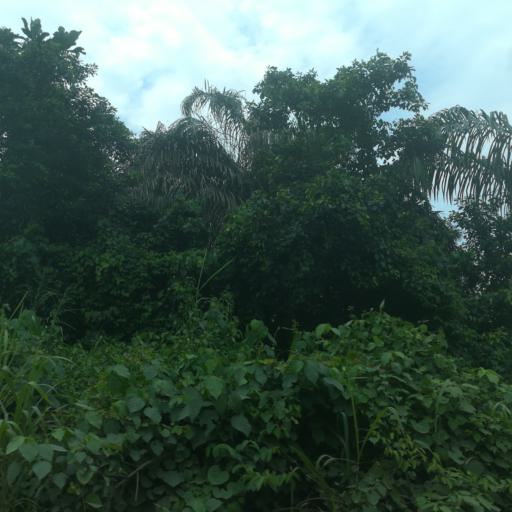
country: NG
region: Lagos
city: Ejirin
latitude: 6.6755
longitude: 3.8005
